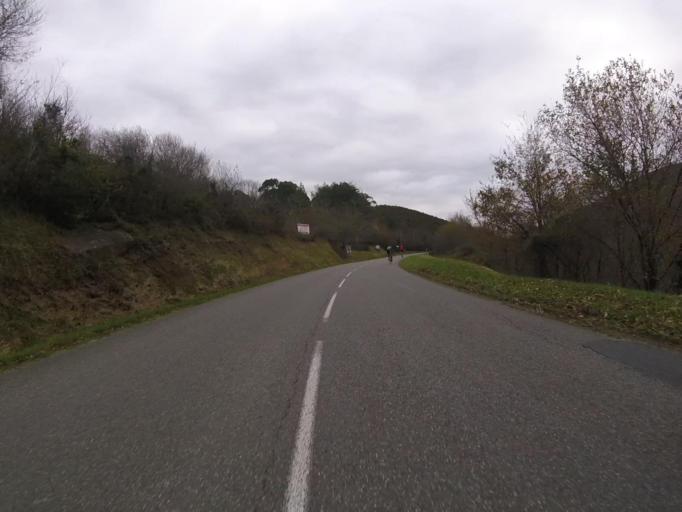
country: FR
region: Aquitaine
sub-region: Departement des Pyrenees-Atlantiques
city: Ascain
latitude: 43.3314
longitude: -1.6031
